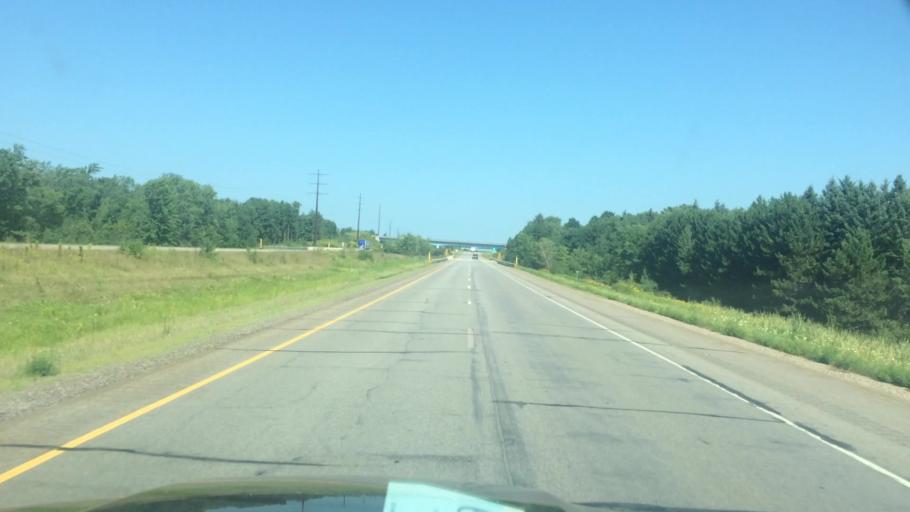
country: US
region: Wisconsin
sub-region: Lincoln County
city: Merrill
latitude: 45.2037
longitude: -89.6576
